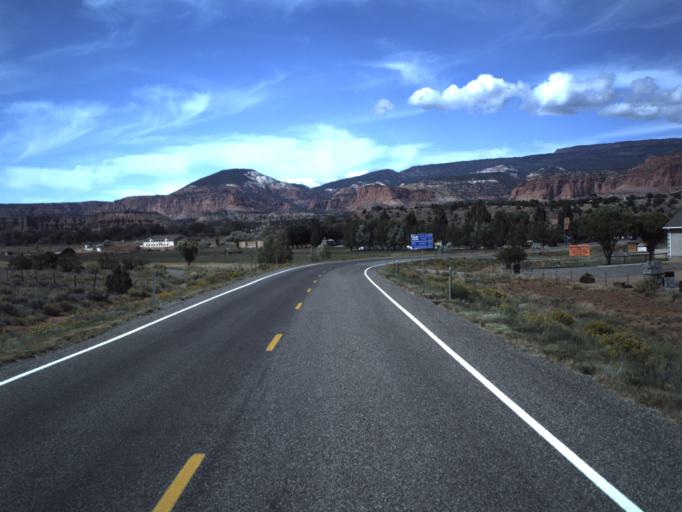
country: US
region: Utah
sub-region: Wayne County
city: Loa
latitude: 38.2951
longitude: -111.3999
